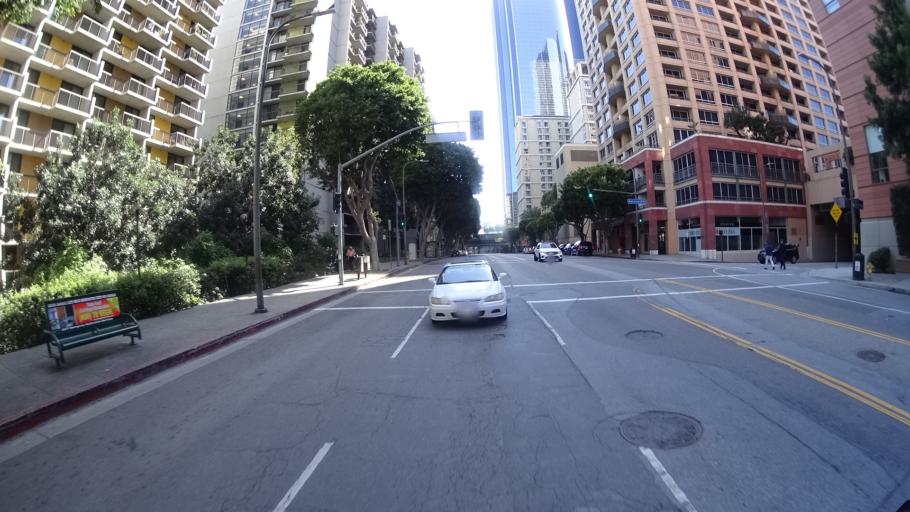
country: US
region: California
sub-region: Los Angeles County
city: Los Angeles
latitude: 34.0533
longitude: -118.2493
